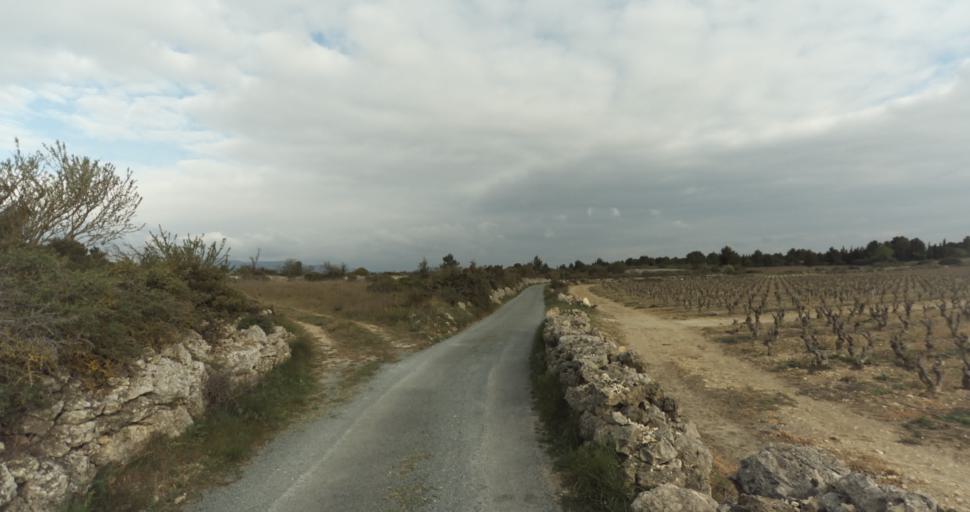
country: FR
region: Languedoc-Roussillon
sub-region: Departement de l'Aude
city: Leucate
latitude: 42.9273
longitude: 3.0250
